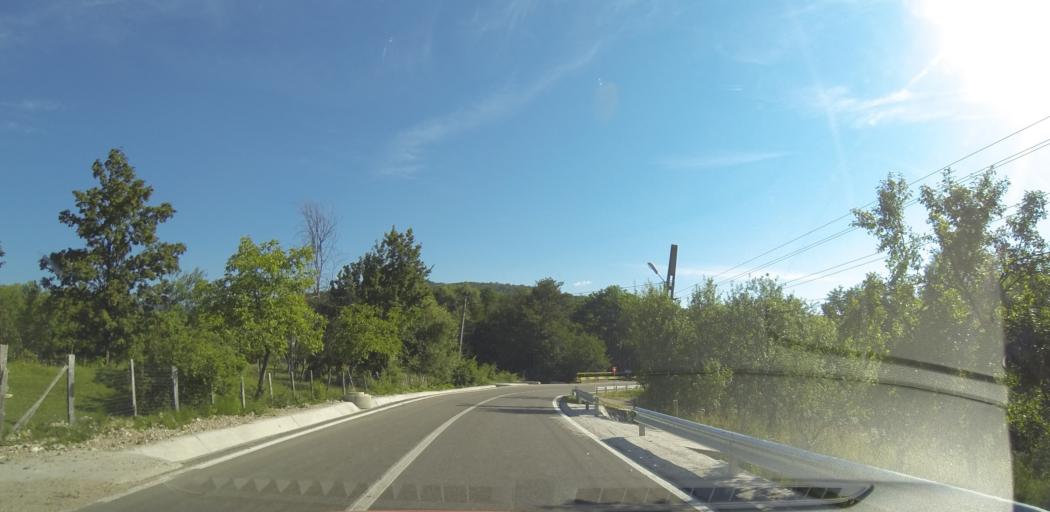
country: RO
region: Valcea
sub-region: Comuna Vaideeni
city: Vaideeni
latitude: 45.1638
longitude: 23.8928
